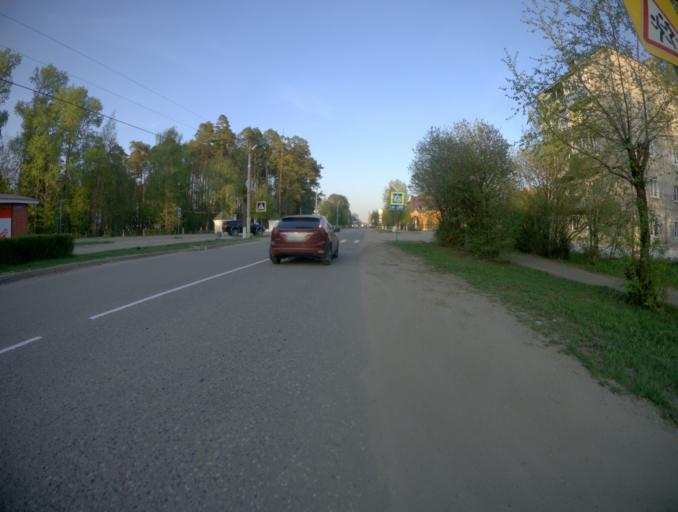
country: RU
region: Ivanovo
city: Yuzha
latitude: 56.5834
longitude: 42.0037
